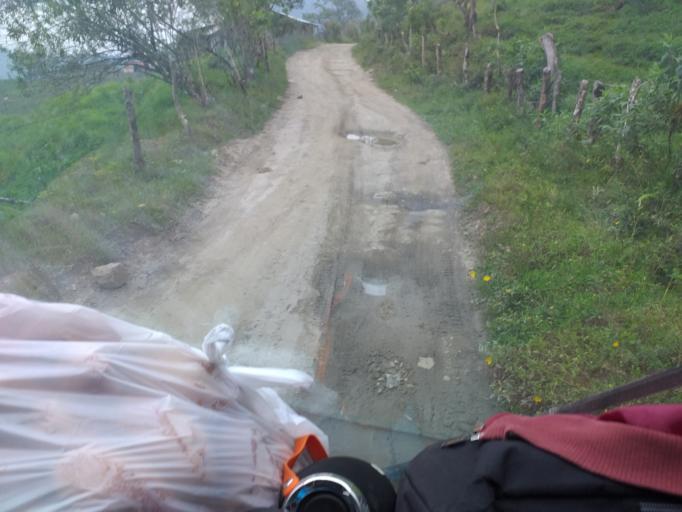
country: CO
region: Boyaca
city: Aquitania
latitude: 5.3240
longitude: -72.9371
